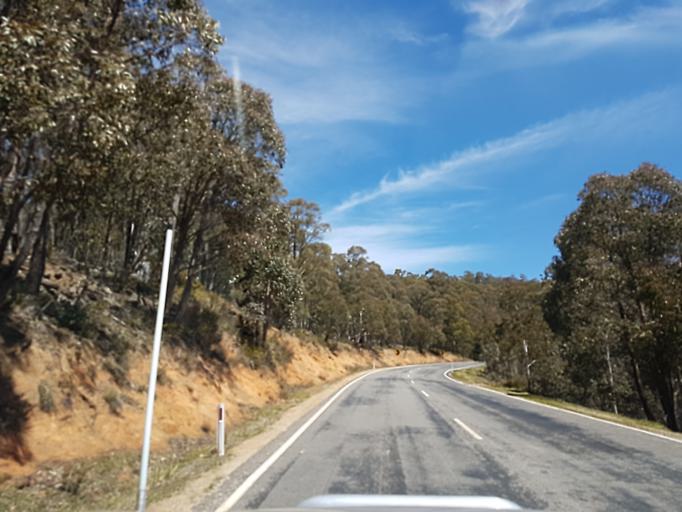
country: AU
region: Victoria
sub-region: Alpine
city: Mount Beauty
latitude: -37.0826
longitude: 147.3771
